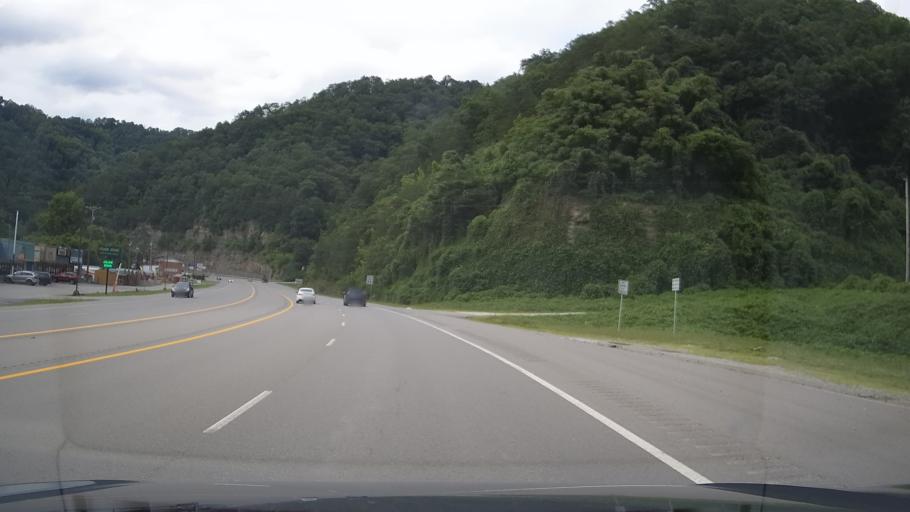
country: US
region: Kentucky
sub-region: Pike County
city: Pikeville
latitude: 37.4442
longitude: -82.5047
